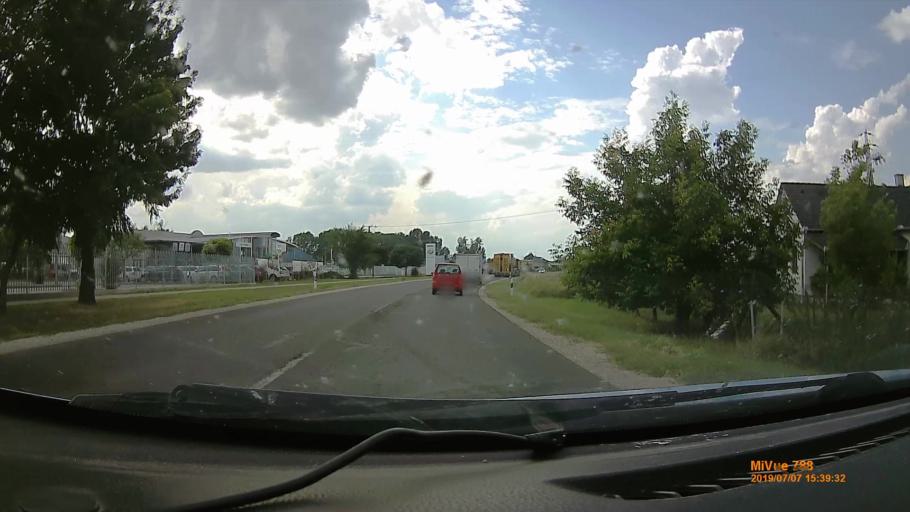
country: HU
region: Jasz-Nagykun-Szolnok
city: Jaszbereny
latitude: 47.4931
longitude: 19.9337
